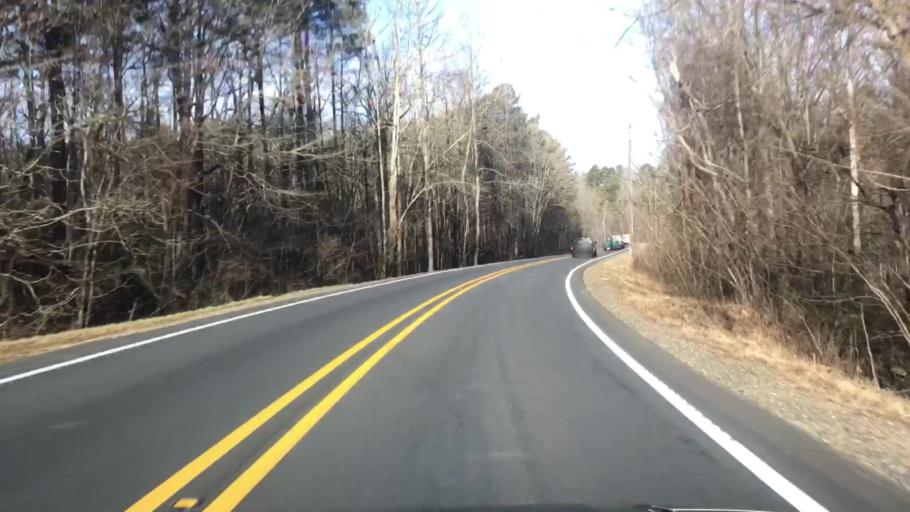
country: US
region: Arkansas
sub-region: Montgomery County
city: Mount Ida
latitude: 34.5231
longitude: -93.3994
